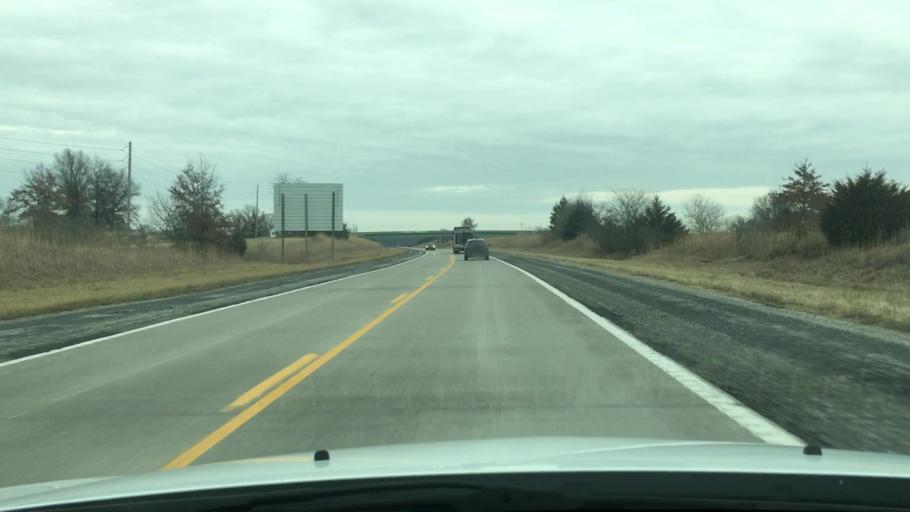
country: US
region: Missouri
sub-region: Audrain County
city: Mexico
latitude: 39.1248
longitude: -91.8717
